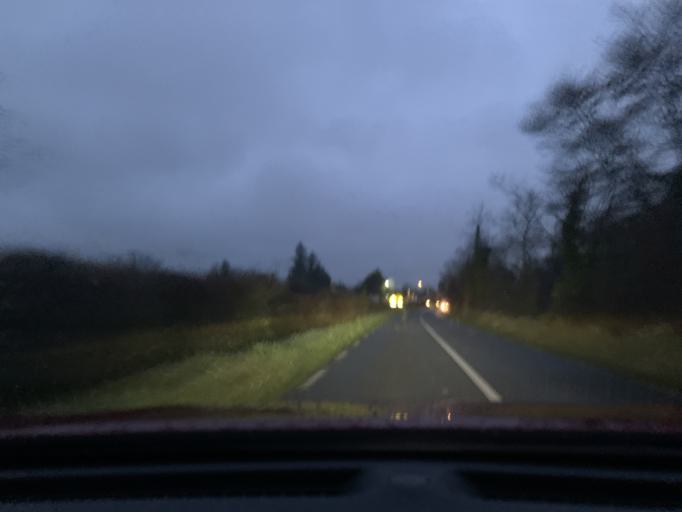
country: IE
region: Connaught
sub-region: Sligo
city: Ballymote
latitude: 54.0810
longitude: -8.5184
